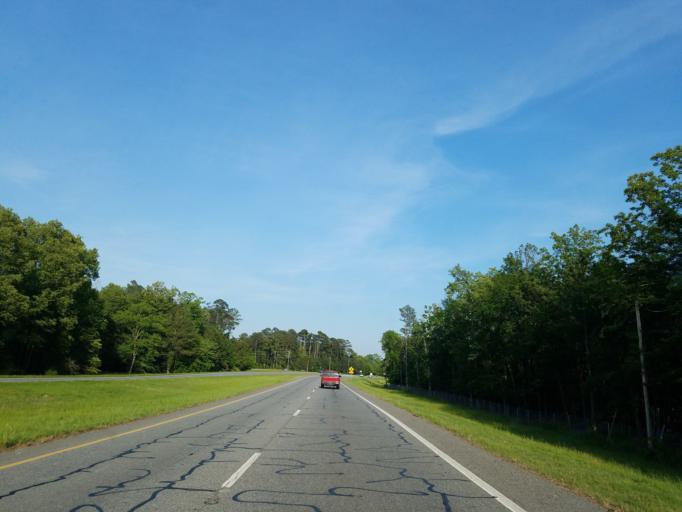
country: US
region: Georgia
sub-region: Floyd County
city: Rome
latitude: 34.3998
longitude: -85.2096
